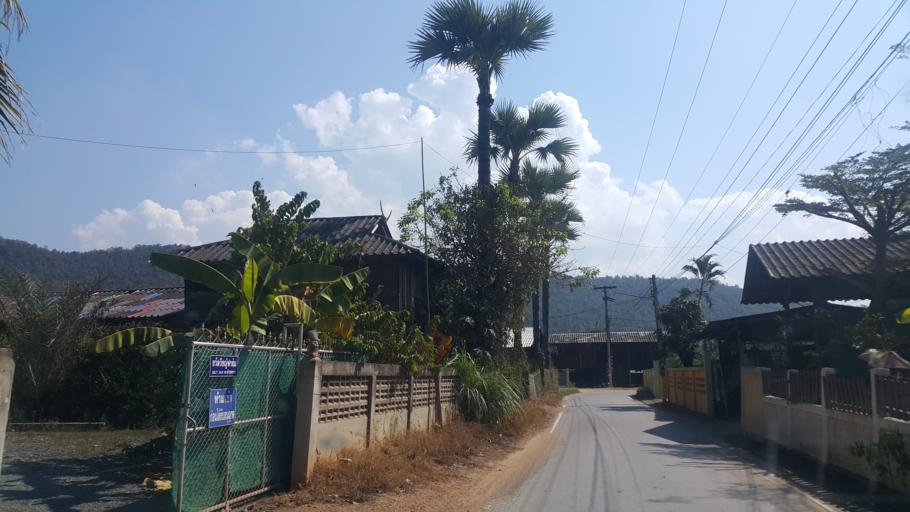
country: TH
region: Chiang Mai
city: San Kamphaeng
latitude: 18.6972
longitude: 99.1648
